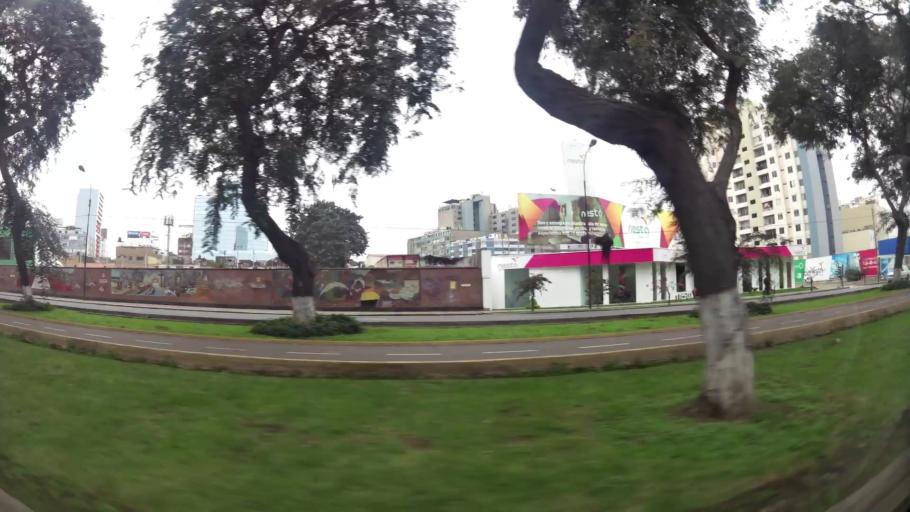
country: PE
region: Lima
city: Lima
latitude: -12.0692
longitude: -77.0399
